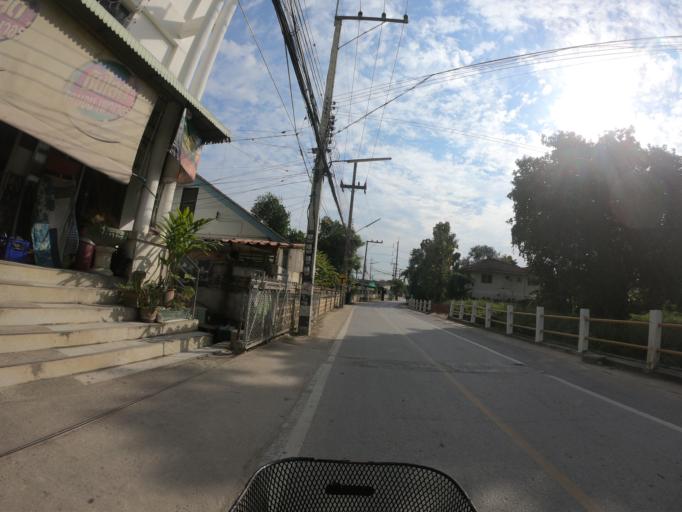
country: TH
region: Chiang Mai
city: Saraphi
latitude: 18.7398
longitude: 99.0437
